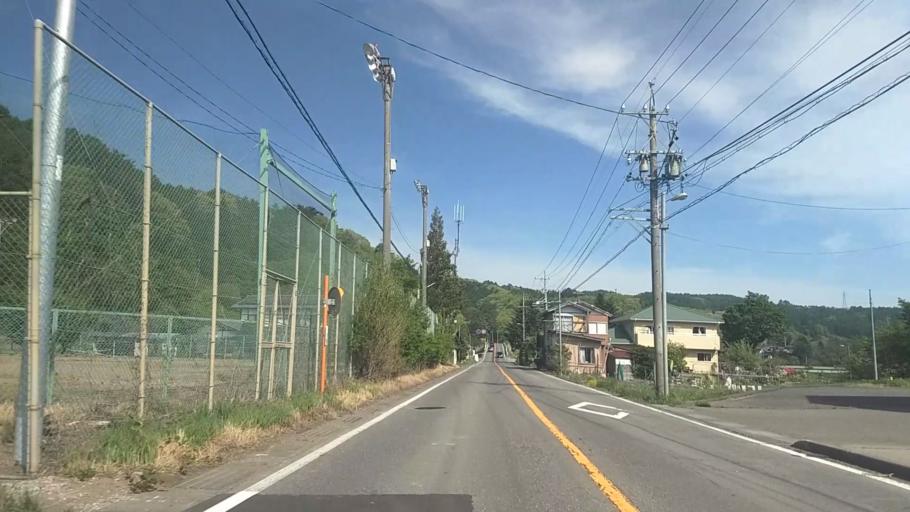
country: JP
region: Nagano
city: Saku
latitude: 36.0363
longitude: 138.4756
